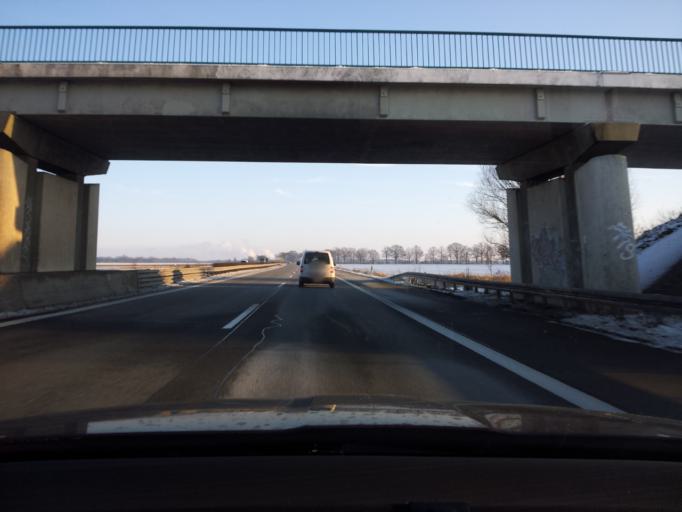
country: DE
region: Brandenburg
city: Heiligengrabe
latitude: 53.1805
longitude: 12.3000
